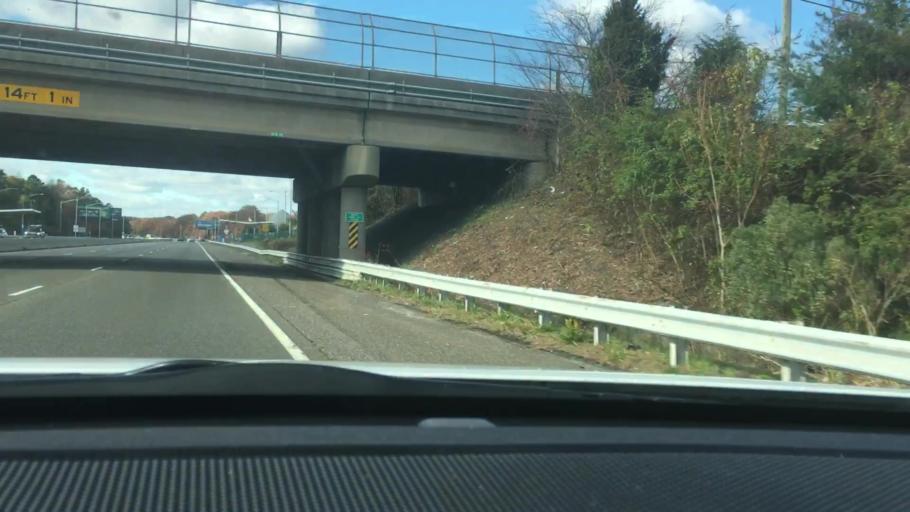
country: US
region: New Jersey
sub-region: Atlantic County
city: Pleasantville
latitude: 39.4021
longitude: -74.5238
